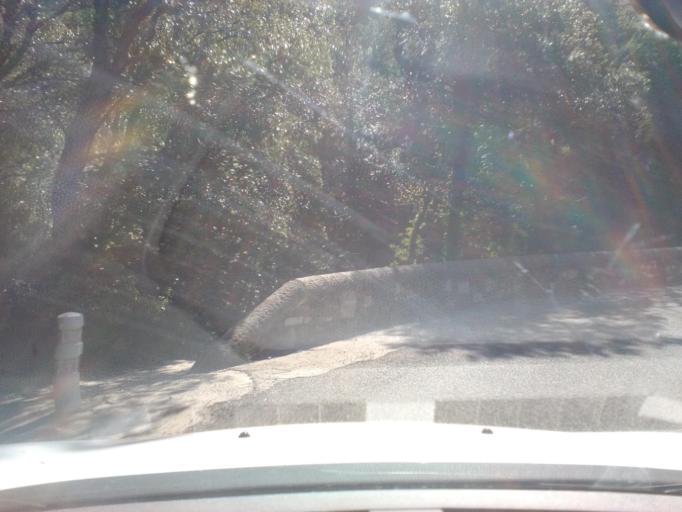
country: FR
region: Languedoc-Roussillon
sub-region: Departement du Gard
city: Saint-Jean-du-Gard
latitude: 44.1379
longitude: 3.7676
